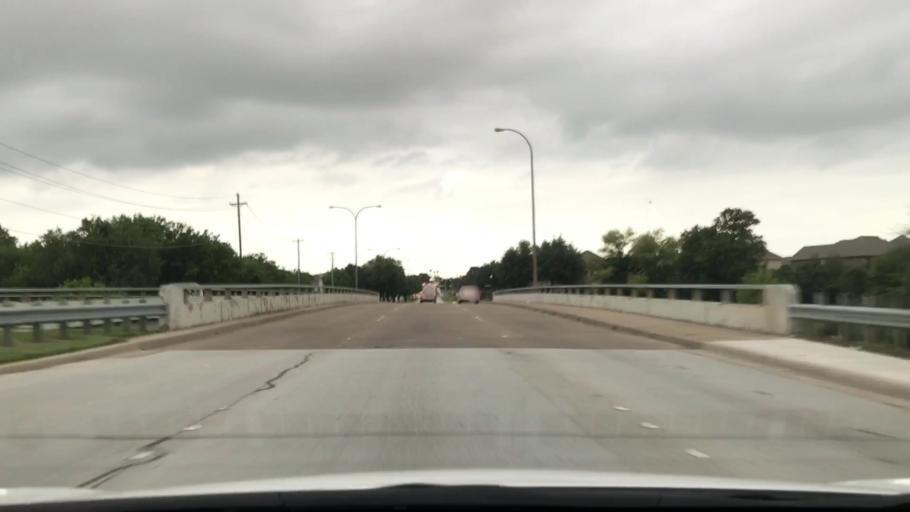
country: US
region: Texas
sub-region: Tarrant County
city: Watauga
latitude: 32.8542
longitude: -97.2901
